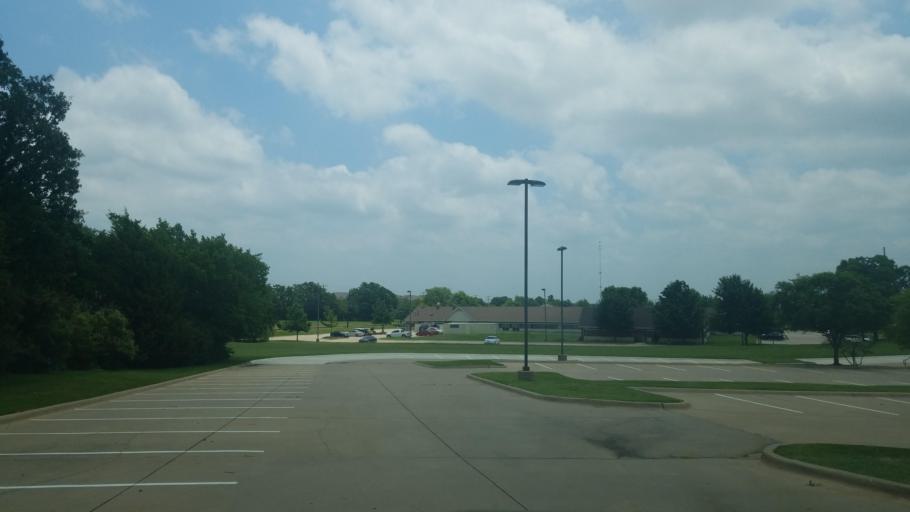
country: US
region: Texas
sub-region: Denton County
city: Denton
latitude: 33.1867
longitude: -97.0991
